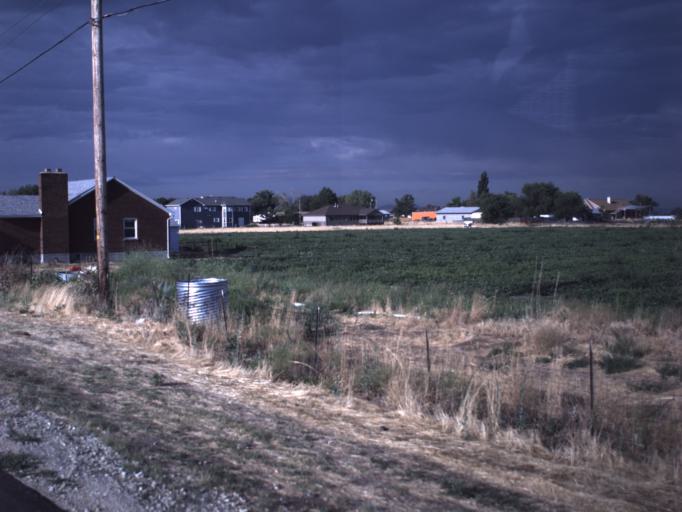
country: US
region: Utah
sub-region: Weber County
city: West Haven
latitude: 41.2078
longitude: -112.0930
